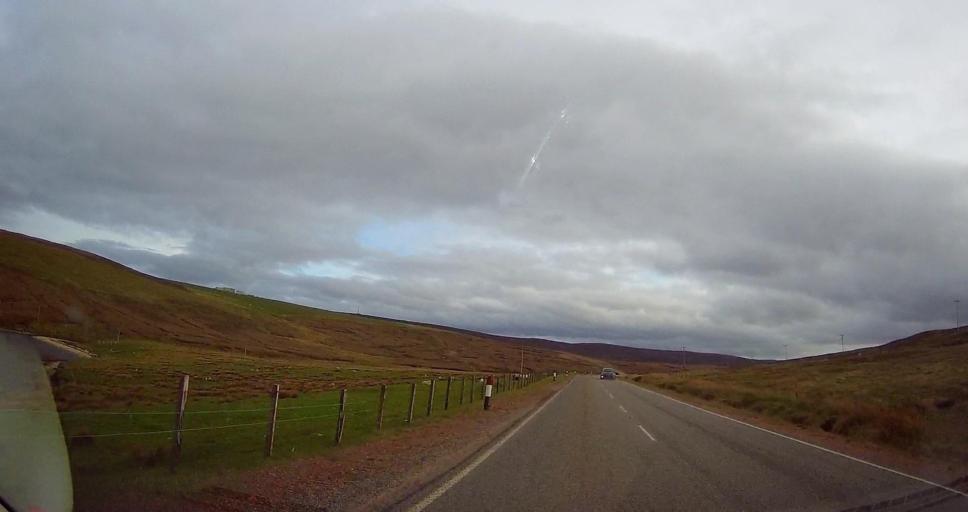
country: GB
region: Scotland
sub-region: Shetland Islands
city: Lerwick
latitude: 60.4598
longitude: -1.2098
